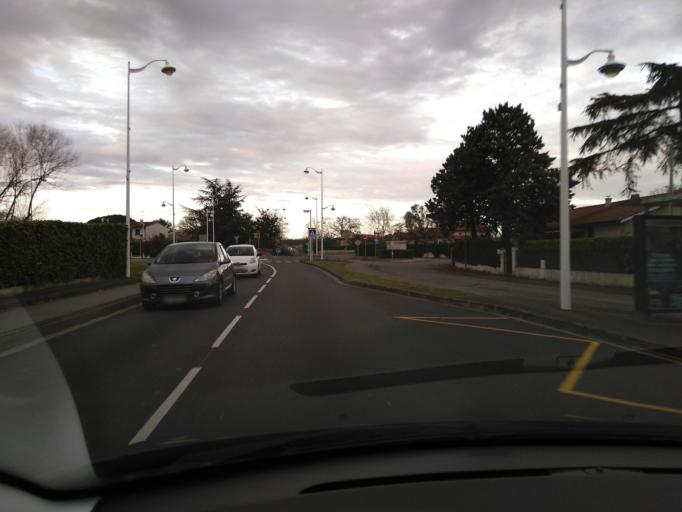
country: FR
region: Midi-Pyrenees
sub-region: Departement de la Haute-Garonne
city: La Salvetat-Saint-Gilles
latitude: 43.5794
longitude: 1.2675
